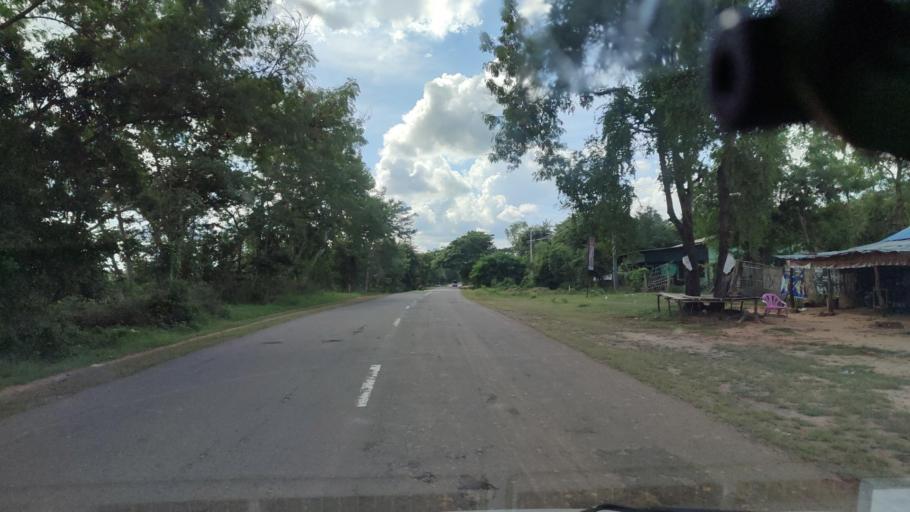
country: MM
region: Mandalay
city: Meiktila
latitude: 20.7888
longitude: 95.5416
